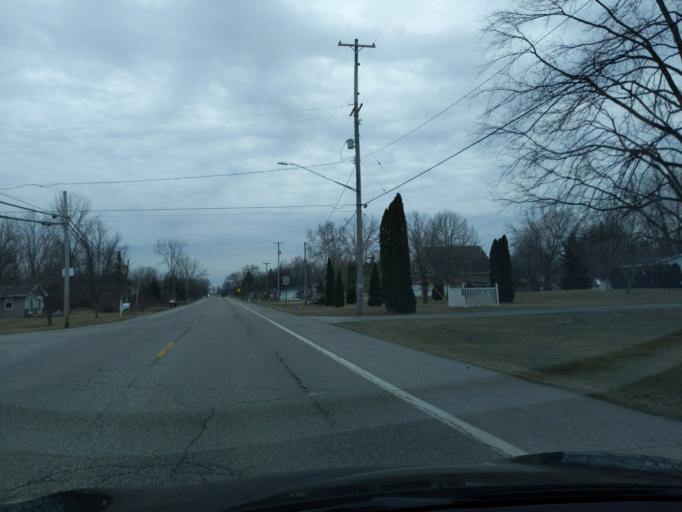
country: US
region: Michigan
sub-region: Bay County
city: Bay City
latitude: 43.6463
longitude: -83.9131
